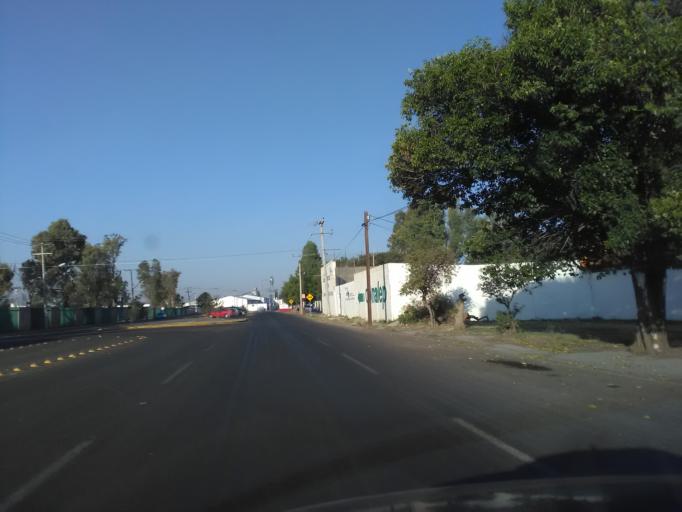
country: MX
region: Durango
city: Victoria de Durango
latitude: 24.0650
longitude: -104.6092
